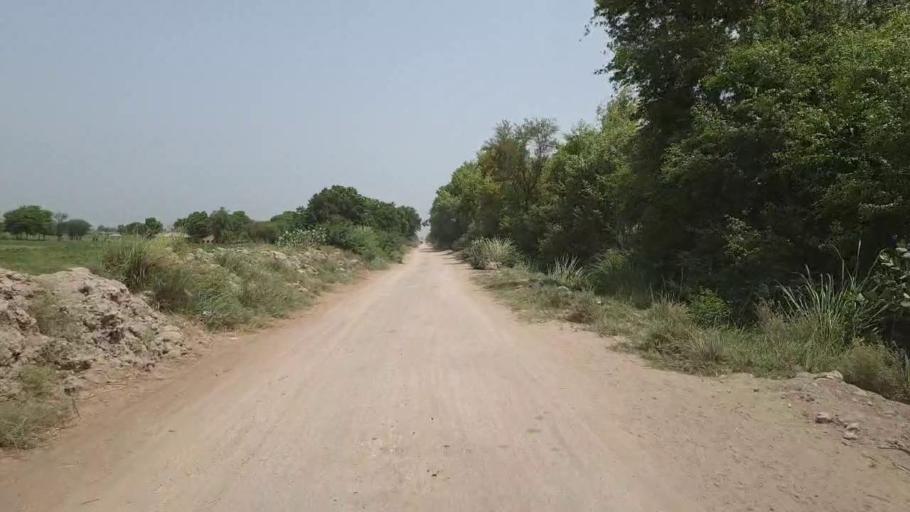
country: PK
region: Sindh
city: Nawabshah
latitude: 26.3143
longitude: 68.3002
